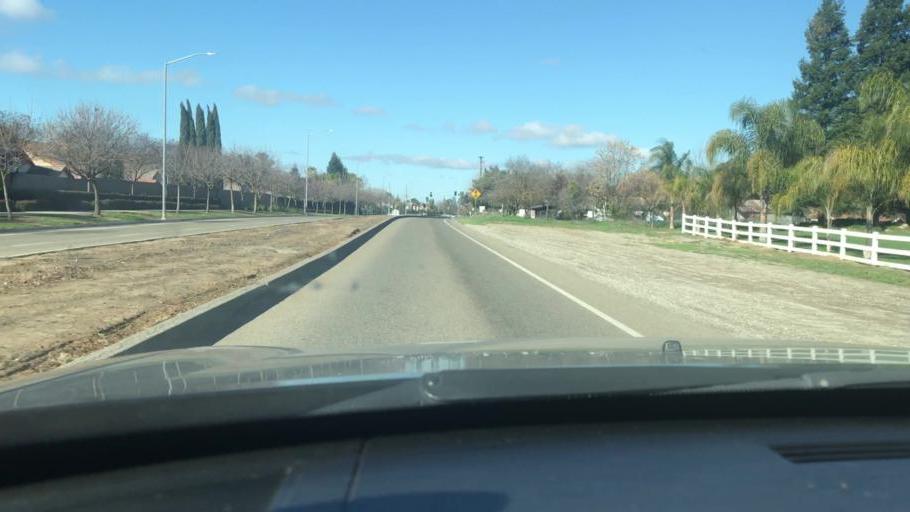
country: US
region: California
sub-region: Fresno County
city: Clovis
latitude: 36.8665
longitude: -119.6812
